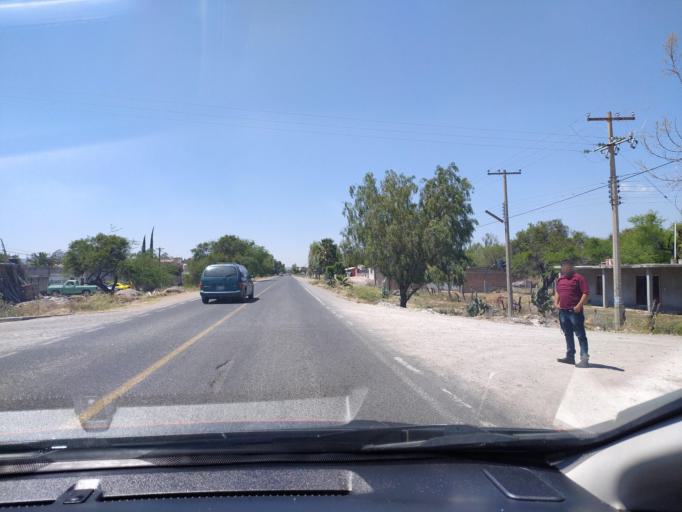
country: MX
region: Guanajuato
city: Ciudad Manuel Doblado
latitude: 20.7406
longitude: -101.8829
